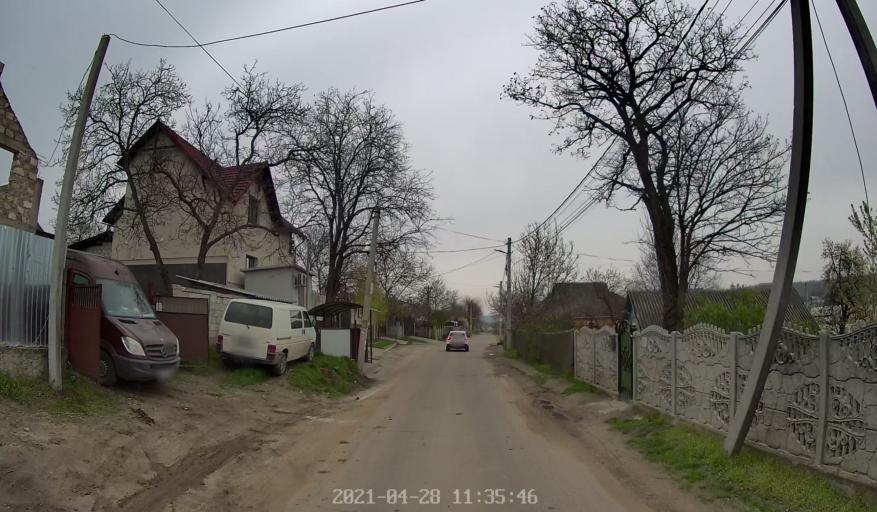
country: MD
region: Chisinau
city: Singera
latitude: 46.9476
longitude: 28.9467
